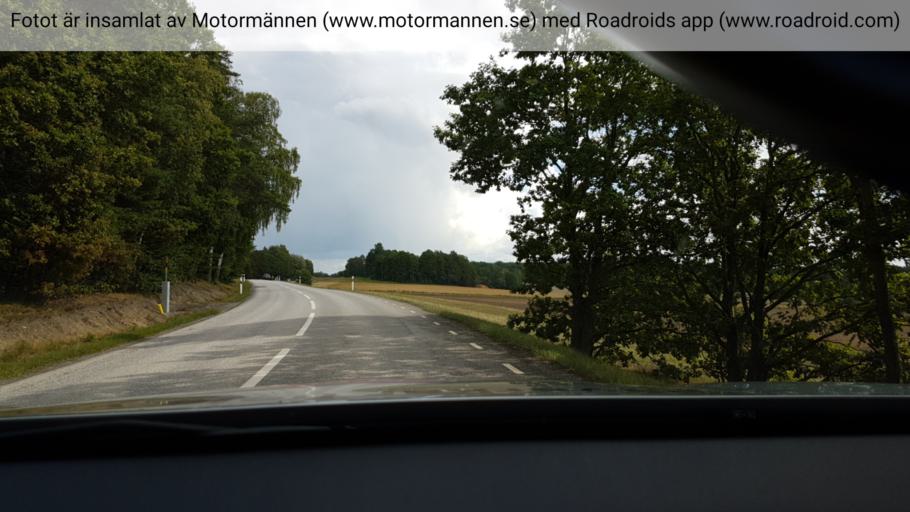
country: SE
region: Stockholm
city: Stenhamra
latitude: 59.2858
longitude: 17.7212
